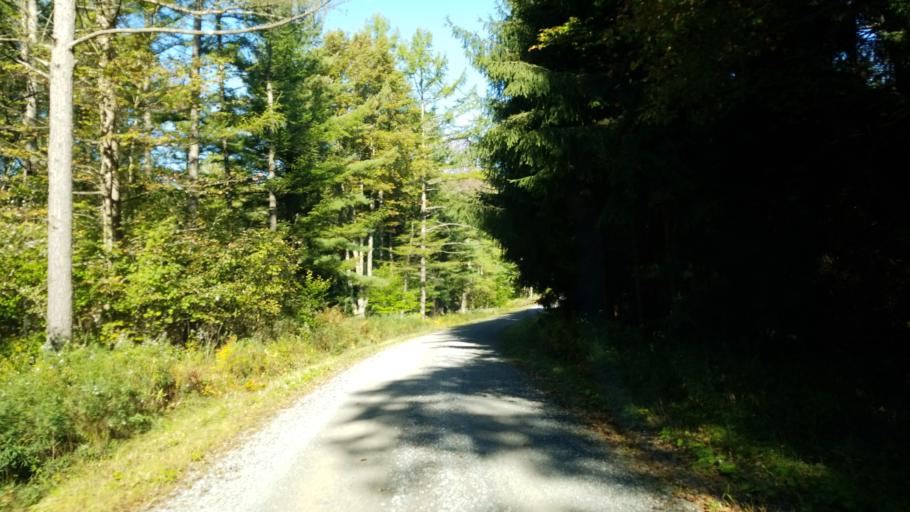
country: US
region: Pennsylvania
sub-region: Clearfield County
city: Treasure Lake
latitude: 41.1367
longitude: -78.5710
